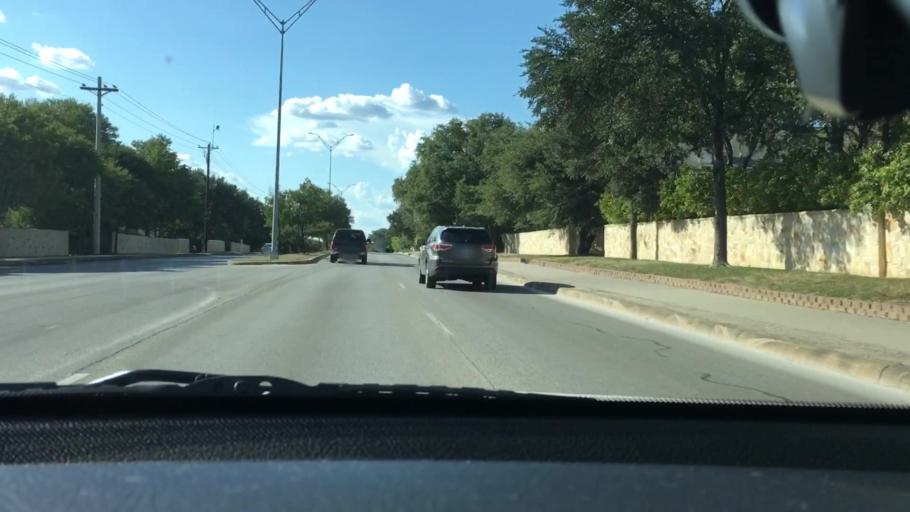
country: US
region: Texas
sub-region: Guadalupe County
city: Schertz
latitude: 29.5749
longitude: -98.2784
